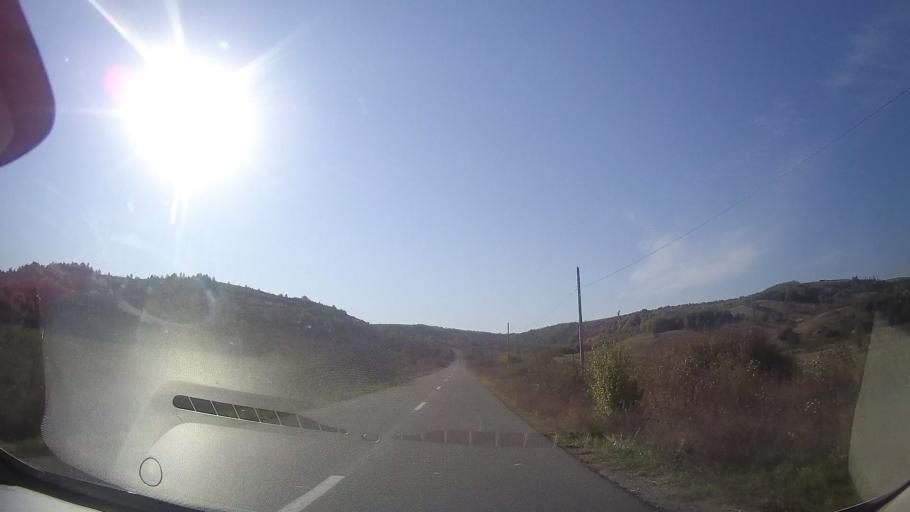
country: RO
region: Timis
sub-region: Oras Recas
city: Recas
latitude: 45.8452
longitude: 21.5199
